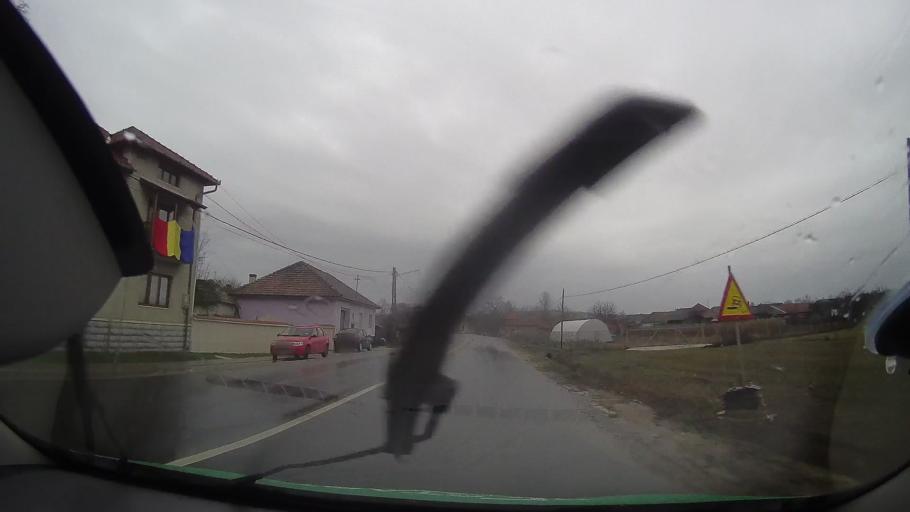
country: RO
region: Bihor
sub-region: Comuna Pocola
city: Pocola
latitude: 46.6930
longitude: 22.2957
